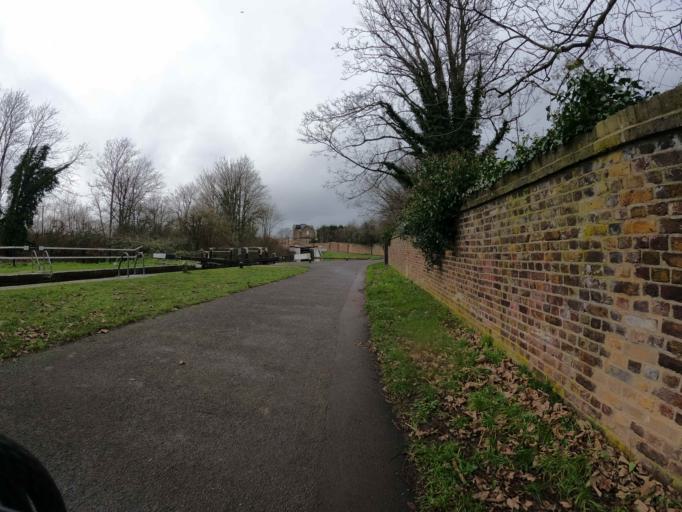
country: GB
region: England
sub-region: Greater London
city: Greenford
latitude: 51.5052
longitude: -0.3465
